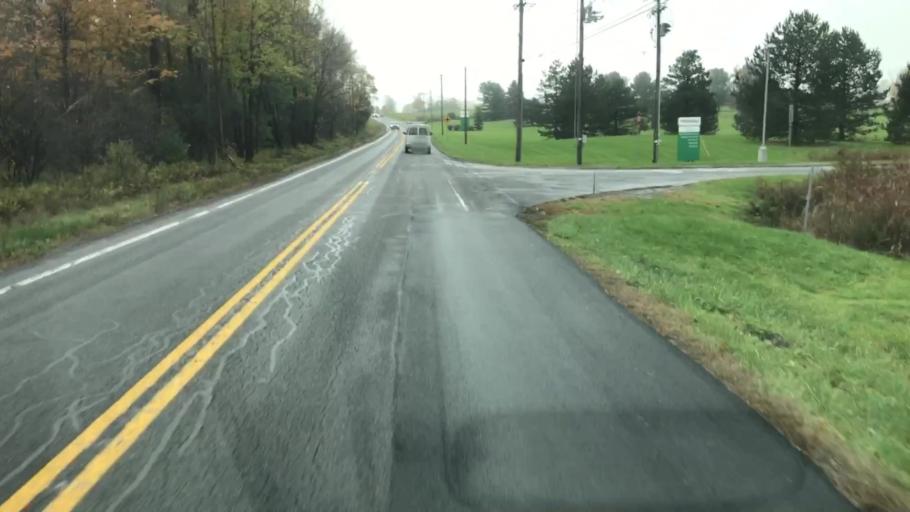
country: US
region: New York
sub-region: Onondaga County
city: Skaneateles
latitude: 42.9788
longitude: -76.4280
